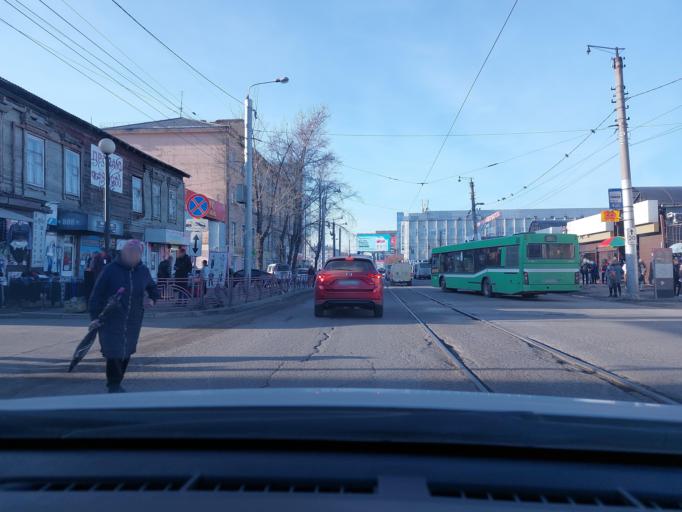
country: RU
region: Irkutsk
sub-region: Irkutskiy Rayon
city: Irkutsk
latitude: 52.2805
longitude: 104.2971
